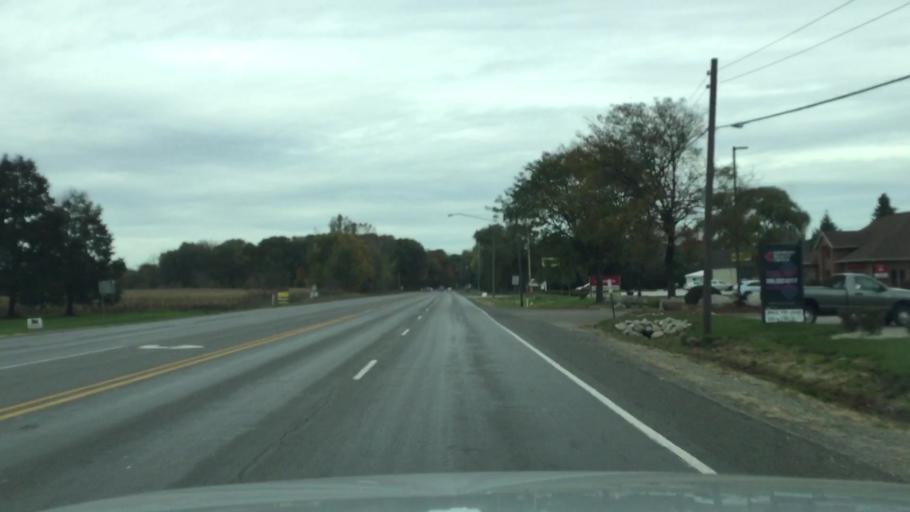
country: US
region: Michigan
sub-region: Kalamazoo County
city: Portage
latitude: 42.2307
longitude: -85.5404
